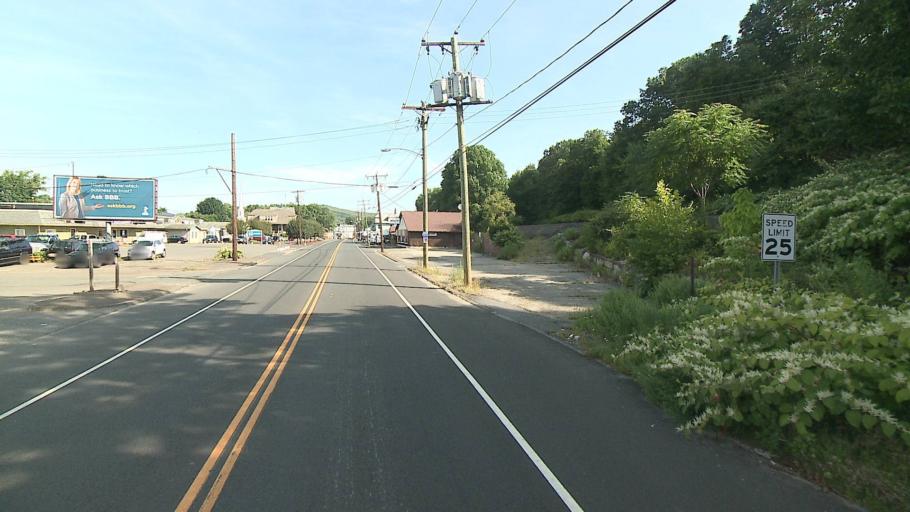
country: US
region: Connecticut
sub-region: New Haven County
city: Waterbury
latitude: 41.5814
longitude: -73.0488
